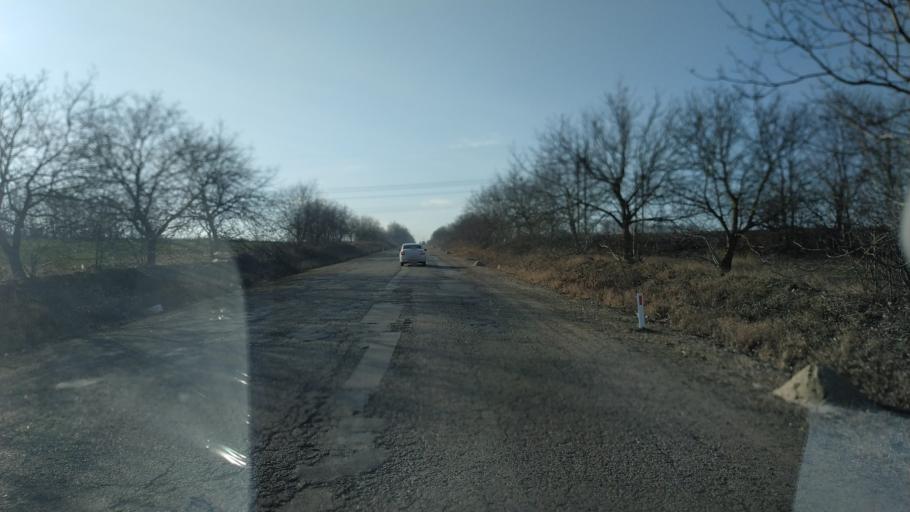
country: MD
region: Chisinau
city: Singera
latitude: 46.8753
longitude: 29.0396
